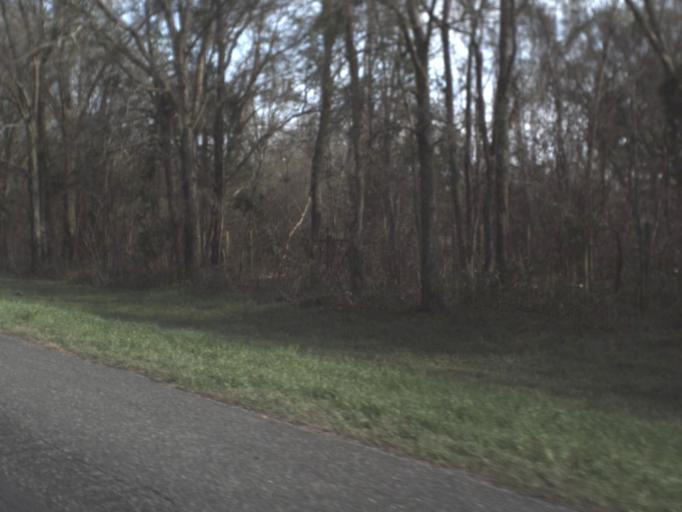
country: US
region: Florida
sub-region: Leon County
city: Tallahassee
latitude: 30.4780
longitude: -84.0861
